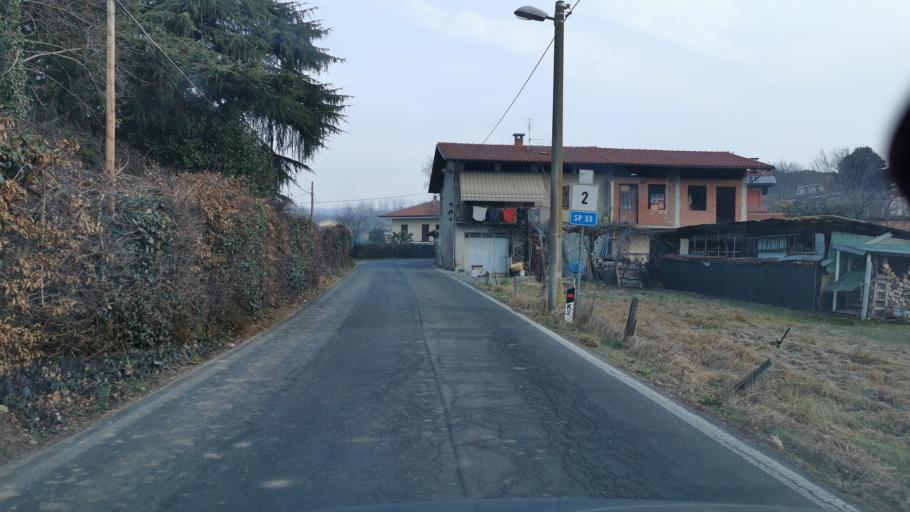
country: IT
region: Piedmont
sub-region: Provincia di Torino
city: Cuceglio
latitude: 45.3511
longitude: 7.8145
